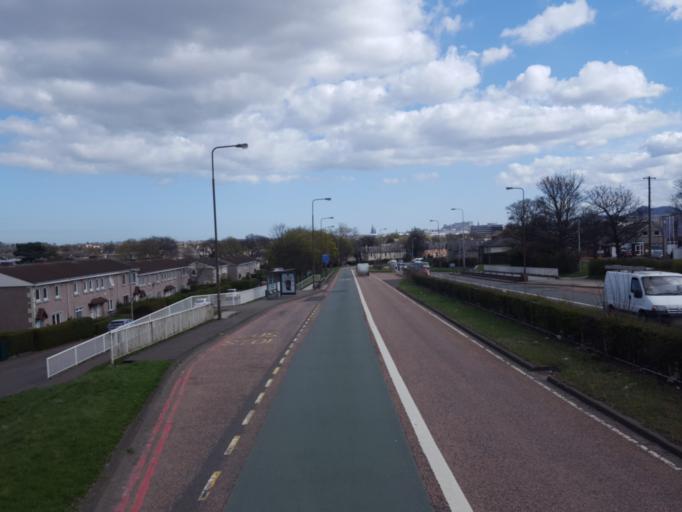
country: GB
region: Scotland
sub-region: Edinburgh
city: Colinton
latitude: 55.9281
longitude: -3.2662
